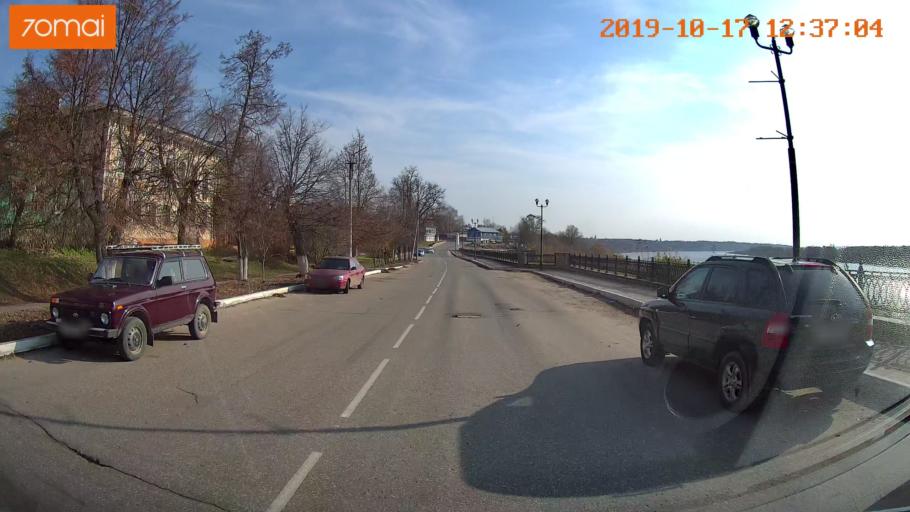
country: RU
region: Rjazan
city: Kasimov
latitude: 54.9377
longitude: 41.3827
